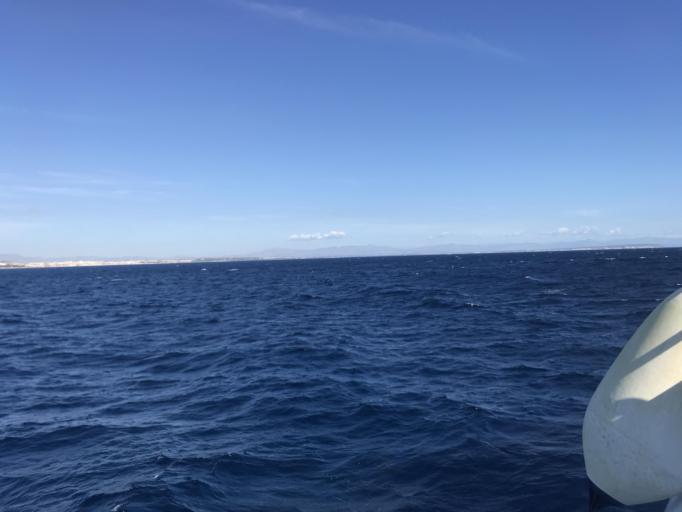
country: ES
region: Valencia
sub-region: Provincia de Alicante
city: Guardamar del Segura
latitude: 38.0316
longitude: -0.6142
